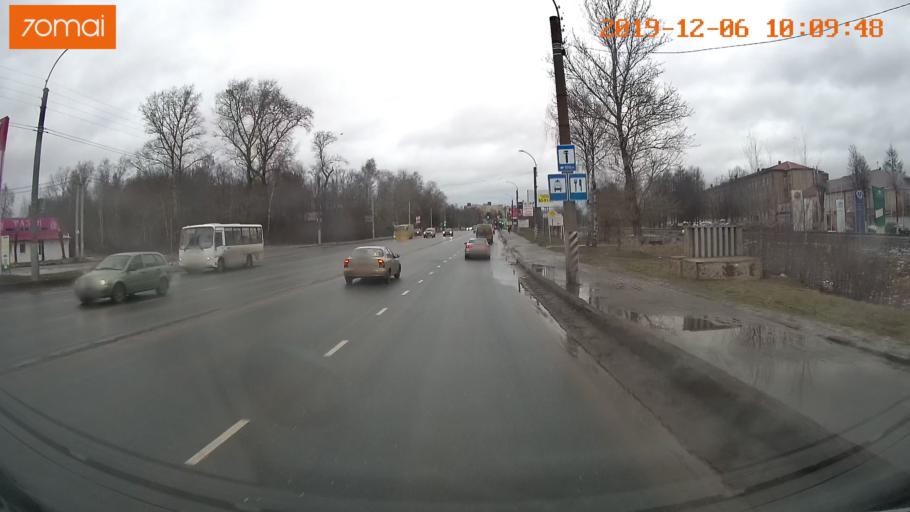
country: RU
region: Ivanovo
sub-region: Gorod Ivanovo
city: Ivanovo
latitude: 57.0266
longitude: 40.9669
